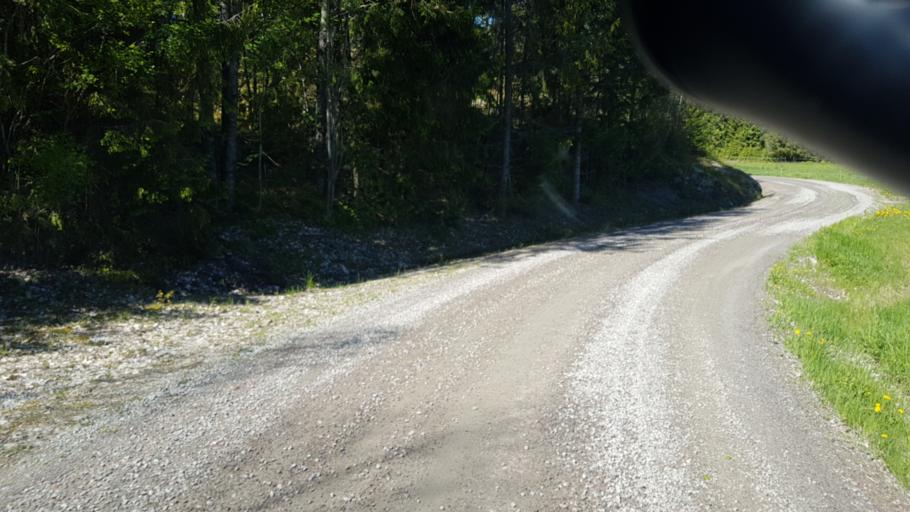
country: SE
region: Vaermland
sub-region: Grums Kommun
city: Grums
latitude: 59.5335
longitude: 12.9075
